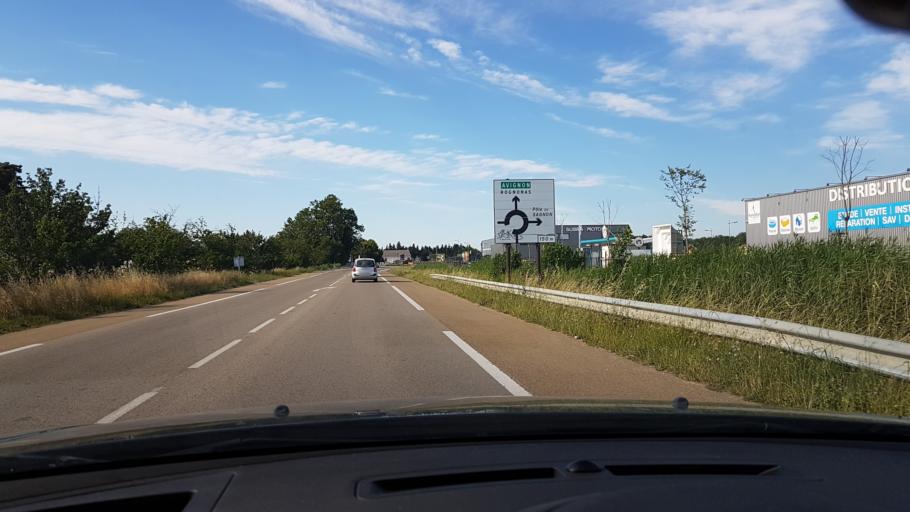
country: FR
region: Provence-Alpes-Cote d'Azur
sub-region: Departement des Bouches-du-Rhone
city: Rognonas
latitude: 43.8848
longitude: 4.7780
